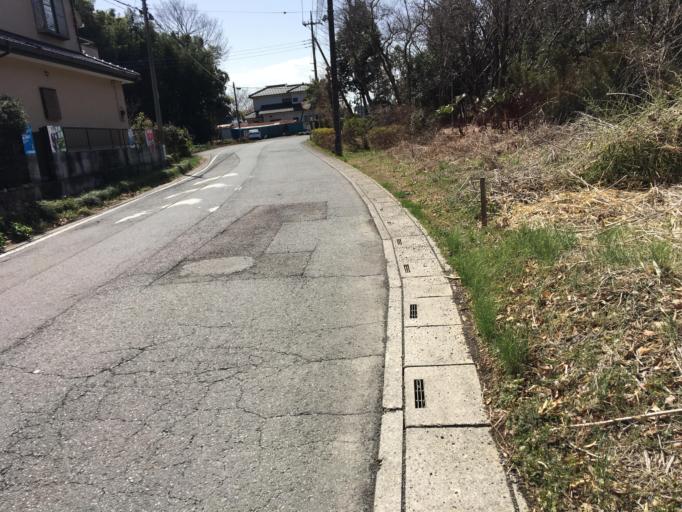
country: JP
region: Saitama
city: Ogawa
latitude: 36.0227
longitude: 139.3289
